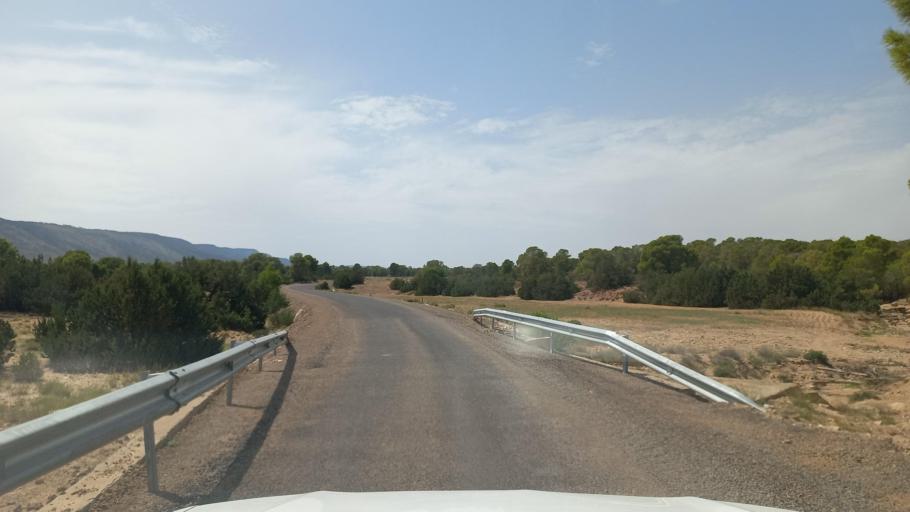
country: TN
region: Al Qasrayn
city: Sbiba
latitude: 35.3857
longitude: 8.9410
